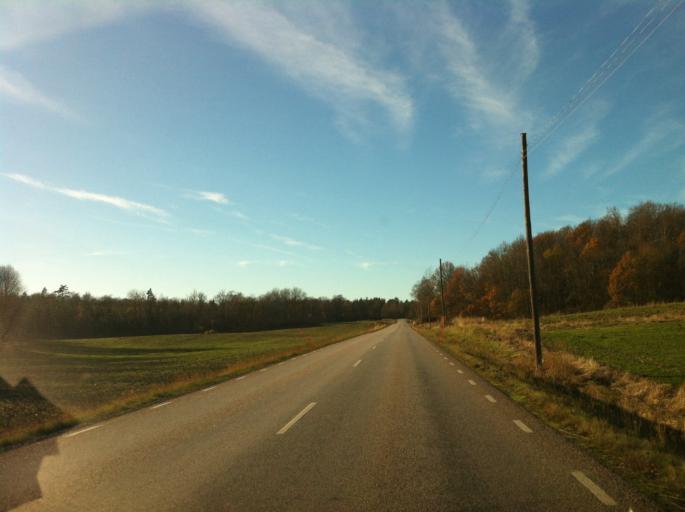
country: SE
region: Blekinge
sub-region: Ronneby Kommun
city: Brakne-Hoby
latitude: 56.2119
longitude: 15.0819
